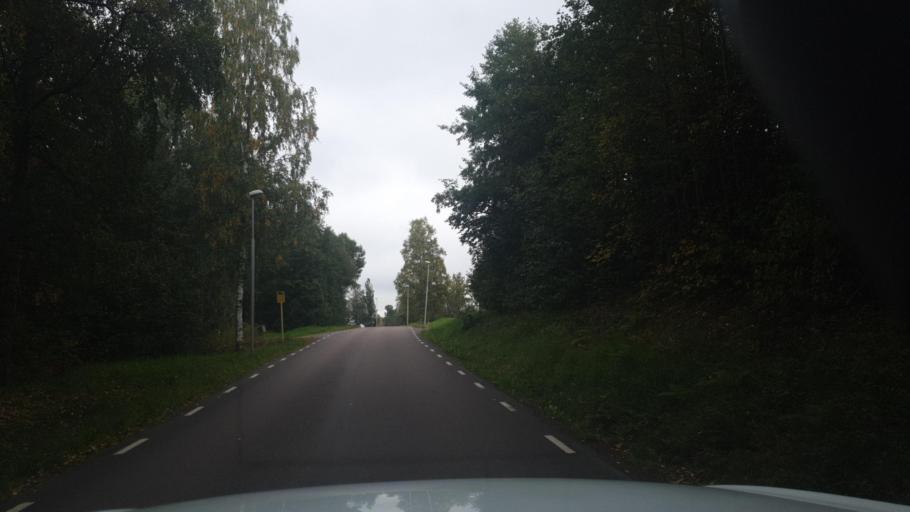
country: SE
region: Vaermland
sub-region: Sunne Kommun
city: Sunne
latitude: 59.8002
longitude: 13.1216
